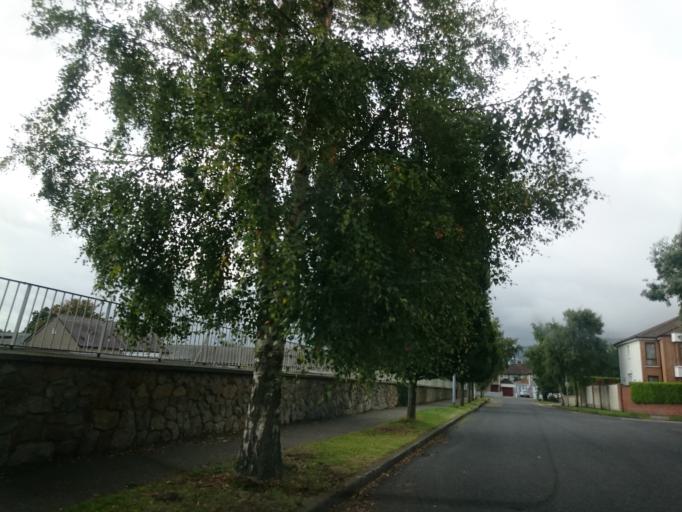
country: IE
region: Leinster
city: Mount Merrion
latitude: 53.2899
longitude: -6.2186
